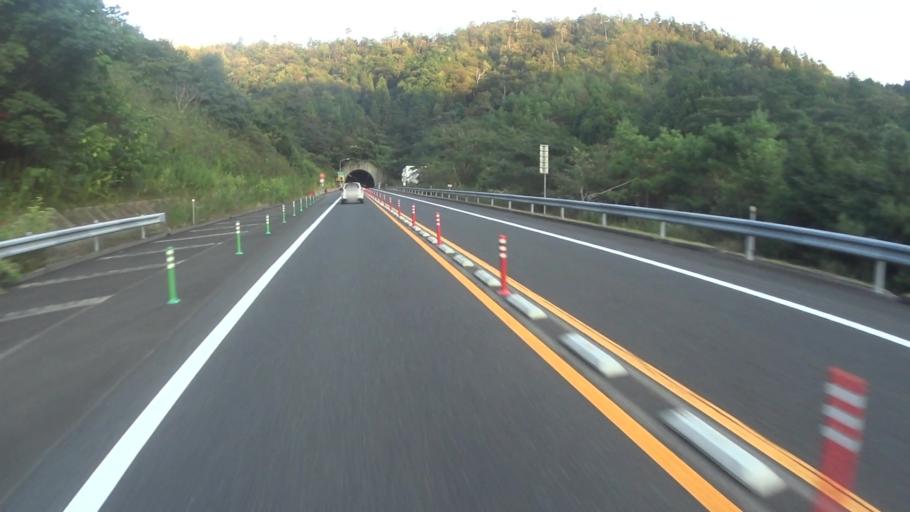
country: JP
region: Kyoto
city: Ayabe
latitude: 35.3803
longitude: 135.2560
